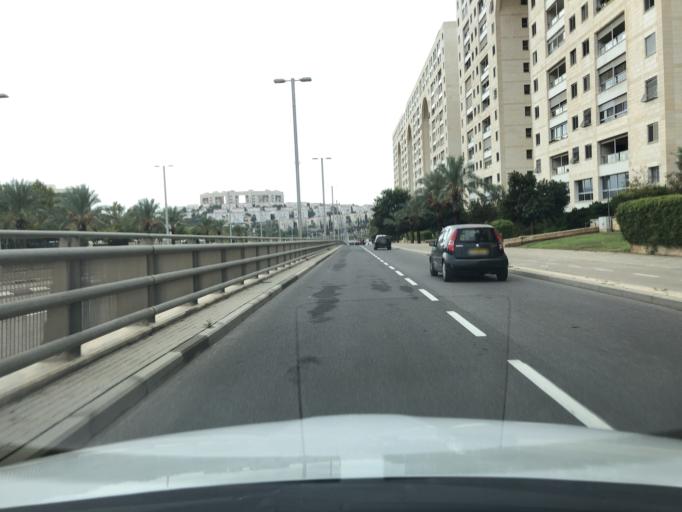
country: IL
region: Central District
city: Modiin
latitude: 31.9052
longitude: 35.0047
